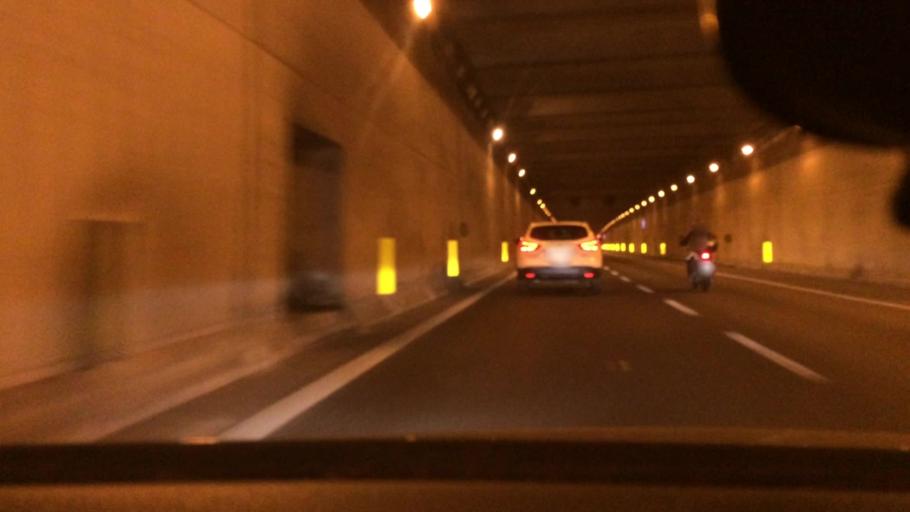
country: IT
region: Lombardy
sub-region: Citta metropolitana di Milano
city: Pero
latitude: 45.5192
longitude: 9.0698
